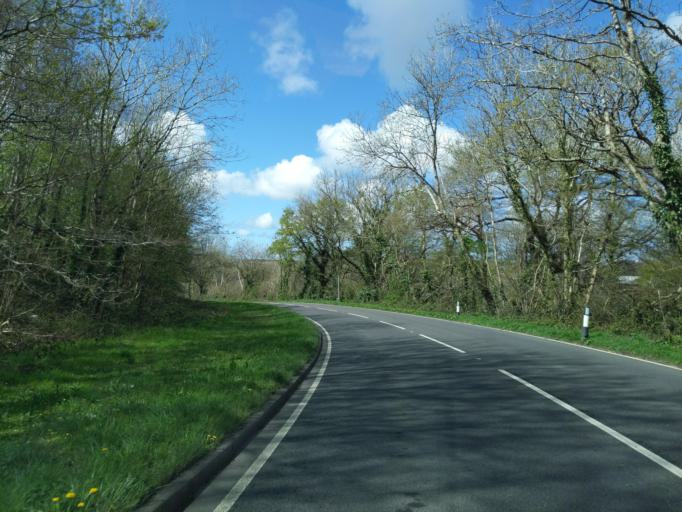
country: GB
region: England
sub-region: Cornwall
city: Helland
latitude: 50.5028
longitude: -4.7764
